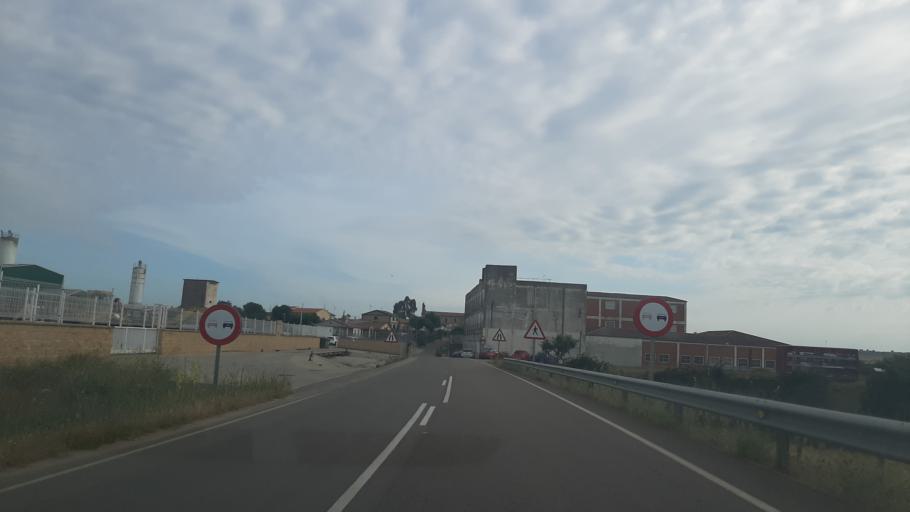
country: ES
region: Castille and Leon
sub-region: Provincia de Salamanca
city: Gallegos de Arganan
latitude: 40.6254
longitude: -6.7036
